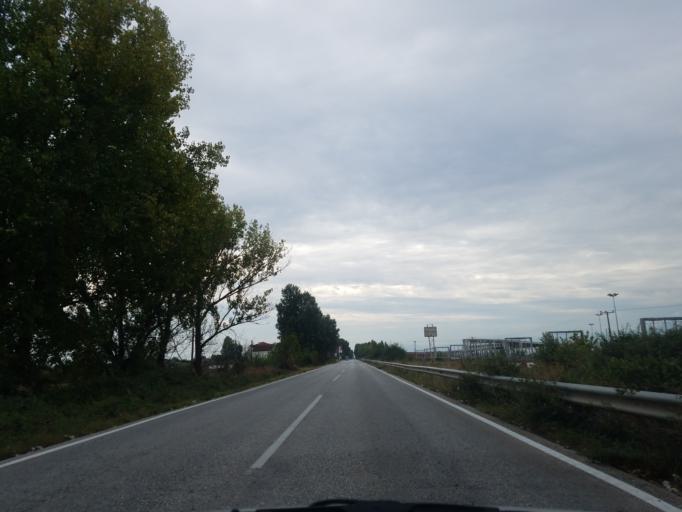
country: GR
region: Thessaly
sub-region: Nomos Kardhitsas
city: Agnantero
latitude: 39.4695
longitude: 21.8498
